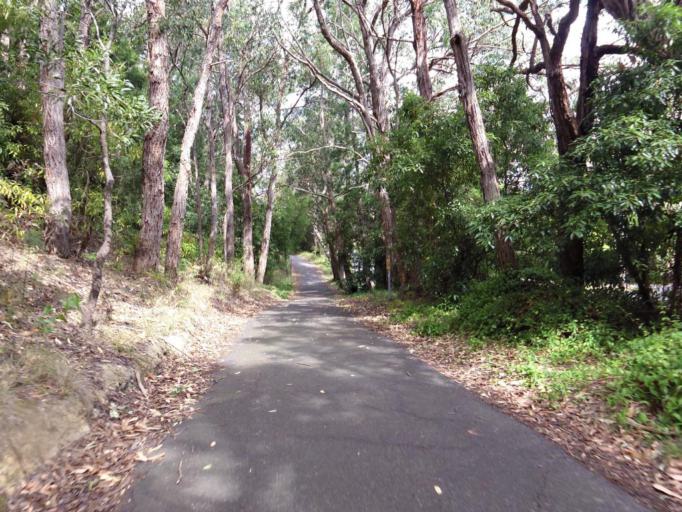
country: AU
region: Victoria
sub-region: Maroondah
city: Heathmont
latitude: -37.8324
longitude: 145.2476
